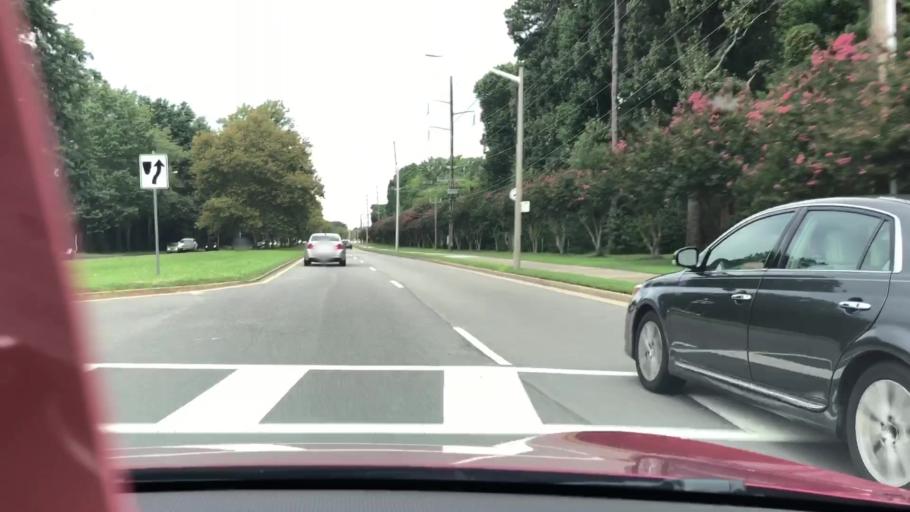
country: US
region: Virginia
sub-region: City of Virginia Beach
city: Virginia Beach
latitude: 36.8919
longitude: -76.0552
